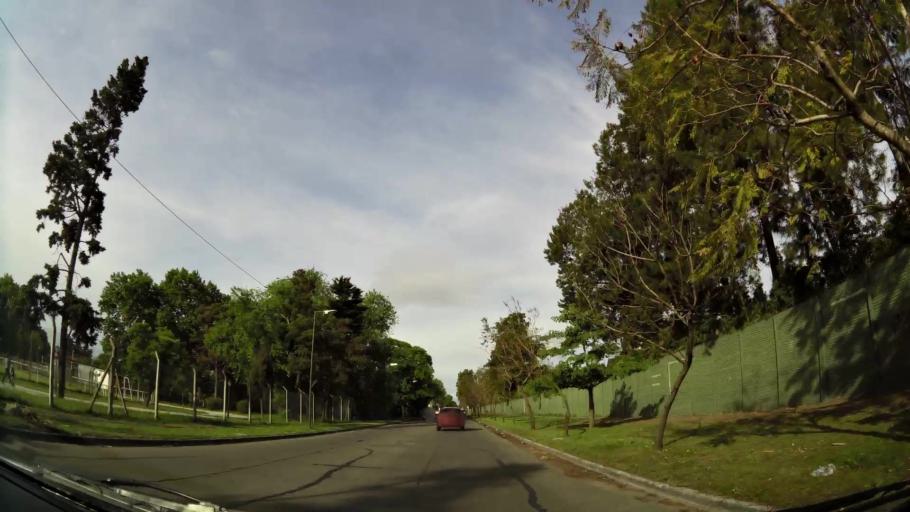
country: AR
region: Buenos Aires
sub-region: Partido de Quilmes
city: Quilmes
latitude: -34.7402
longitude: -58.2566
